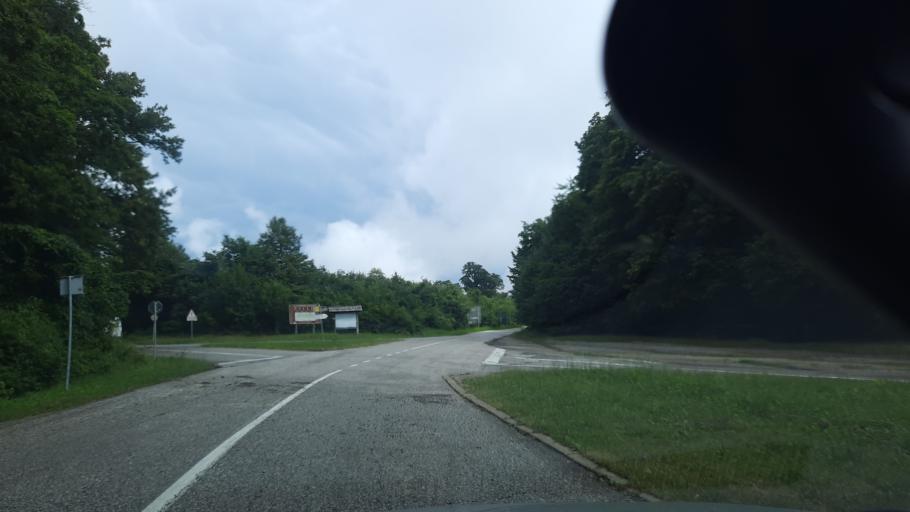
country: RS
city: Glozan
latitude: 45.1451
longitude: 19.5790
